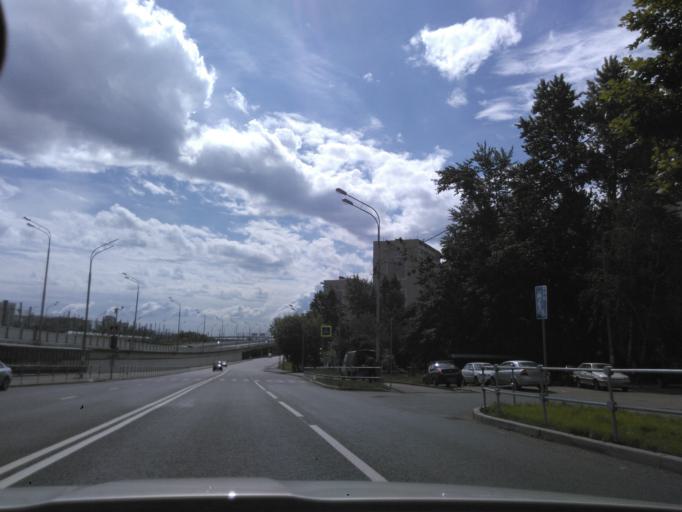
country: RU
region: Moscow
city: Businovo
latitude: 55.8756
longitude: 37.4934
